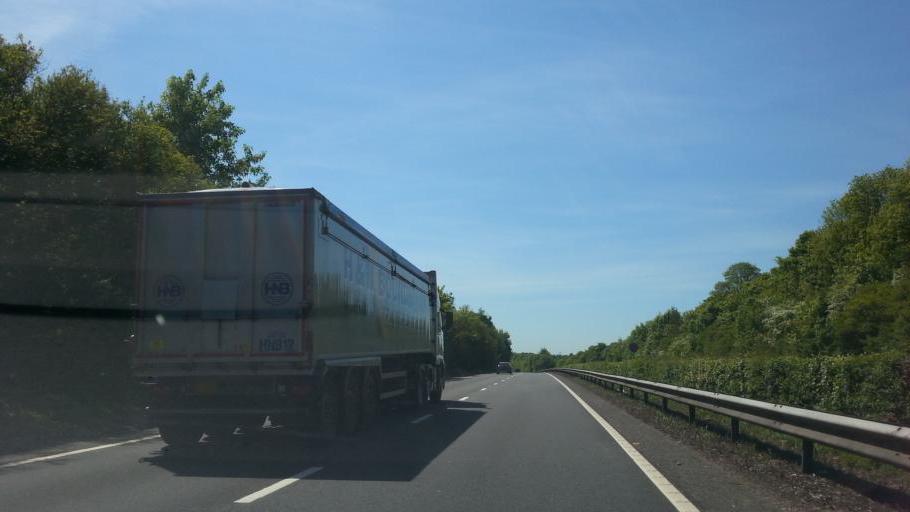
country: GB
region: England
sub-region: Hampshire
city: Overton
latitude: 51.1776
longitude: -1.3183
